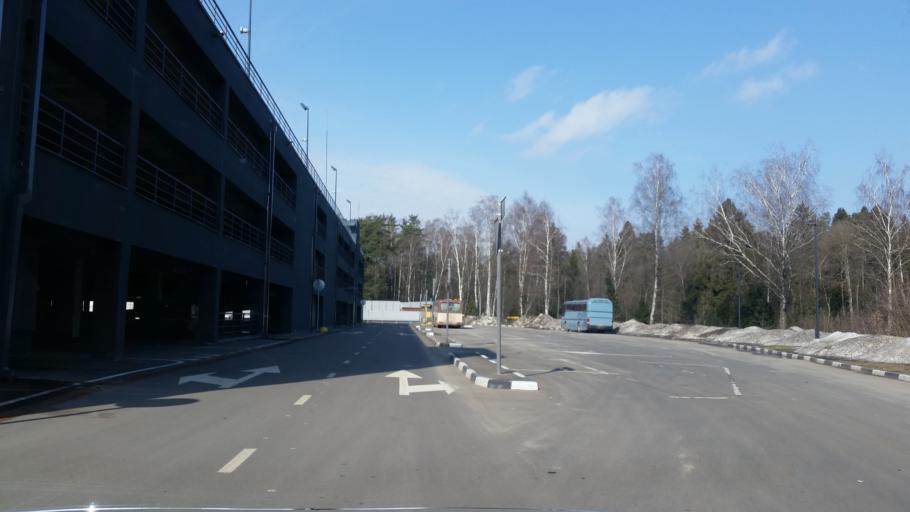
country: RU
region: Moskovskaya
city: Arkhangel'skoye
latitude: 55.8002
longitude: 37.2775
